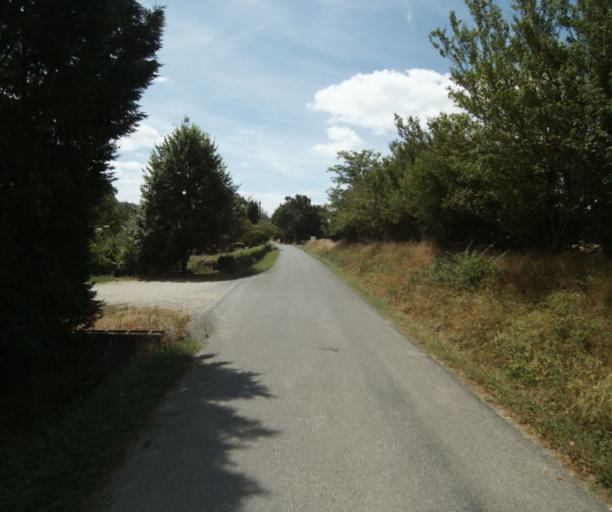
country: FR
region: Midi-Pyrenees
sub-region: Departement du Tarn
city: Soreze
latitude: 43.4869
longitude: 2.0776
